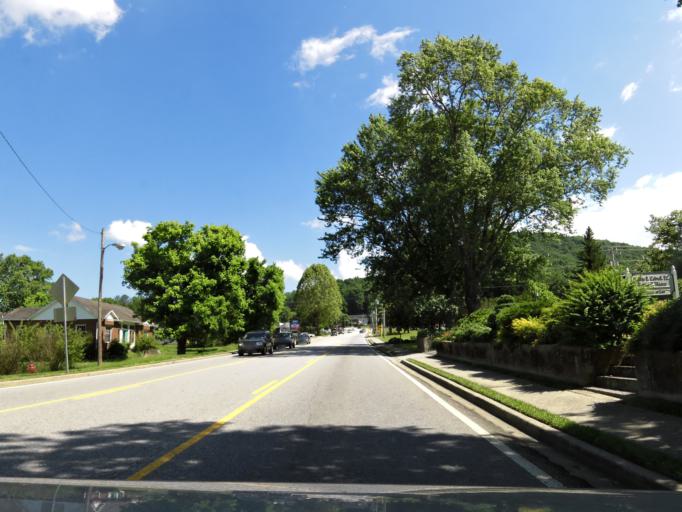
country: US
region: Georgia
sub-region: Union County
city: Blairsville
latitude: 34.8740
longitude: -83.9571
